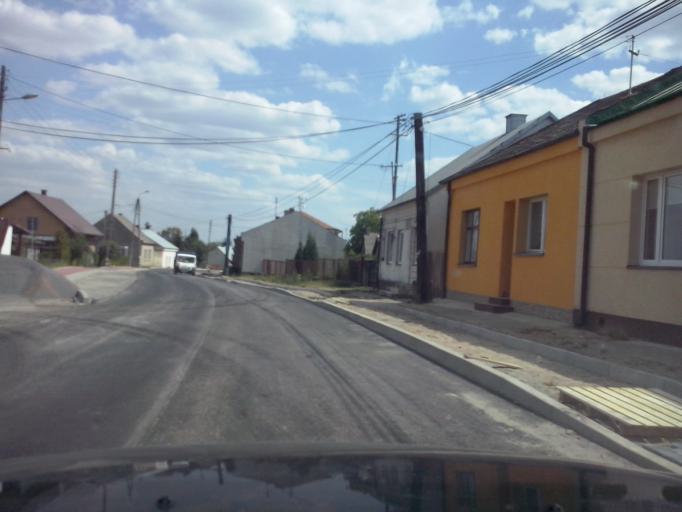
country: PL
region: Swietokrzyskie
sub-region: Powiat staszowski
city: Staszow
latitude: 50.5901
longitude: 21.1023
